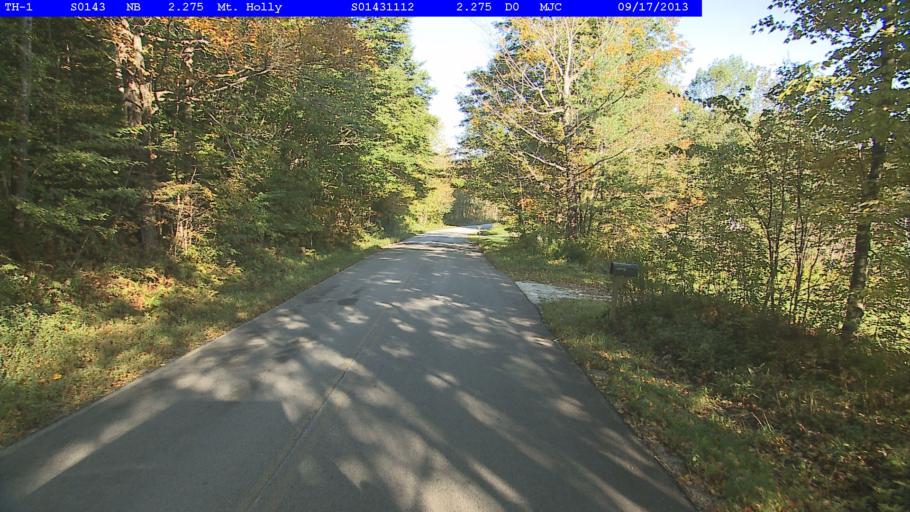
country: US
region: Vermont
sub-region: Rutland County
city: Rutland
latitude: 43.4310
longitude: -72.8232
